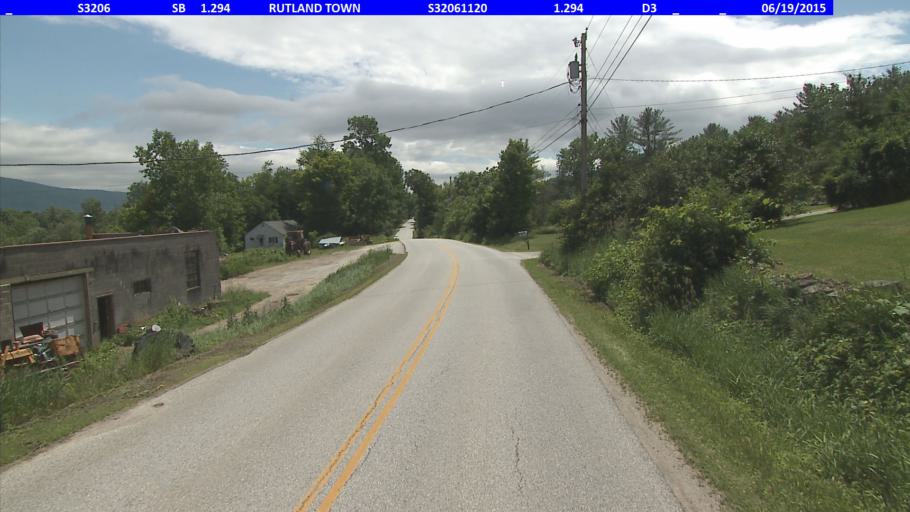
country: US
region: Vermont
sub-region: Rutland County
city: Rutland
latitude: 43.6473
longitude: -72.9959
